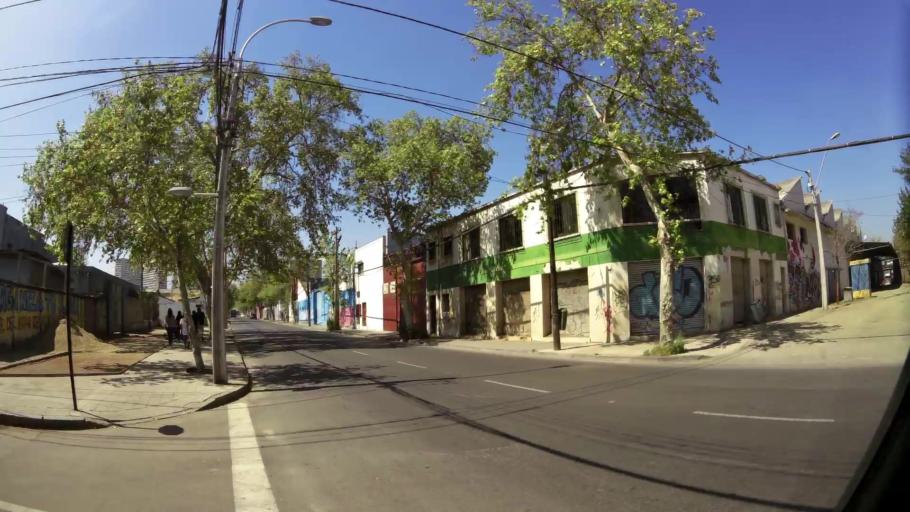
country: CL
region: Santiago Metropolitan
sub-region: Provincia de Santiago
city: Santiago
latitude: -33.4720
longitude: -70.6311
